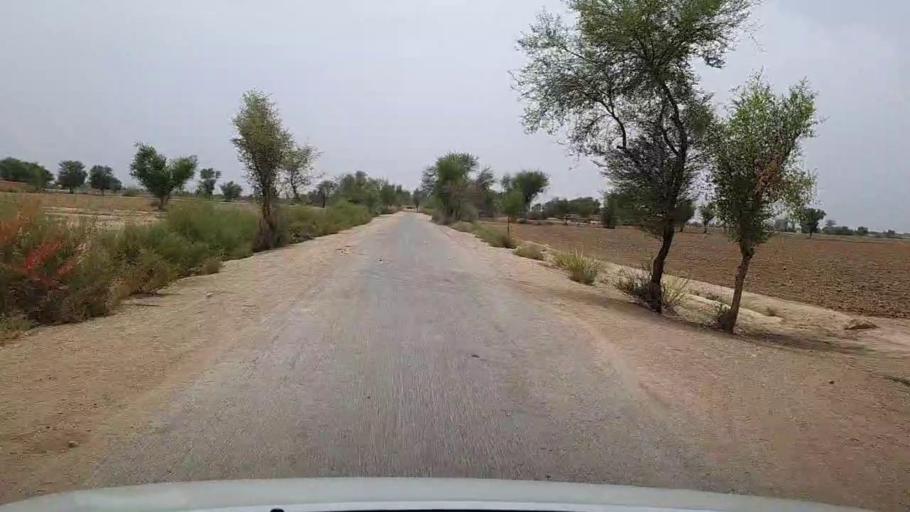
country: PK
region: Sindh
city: Sehwan
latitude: 26.3159
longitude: 67.7534
